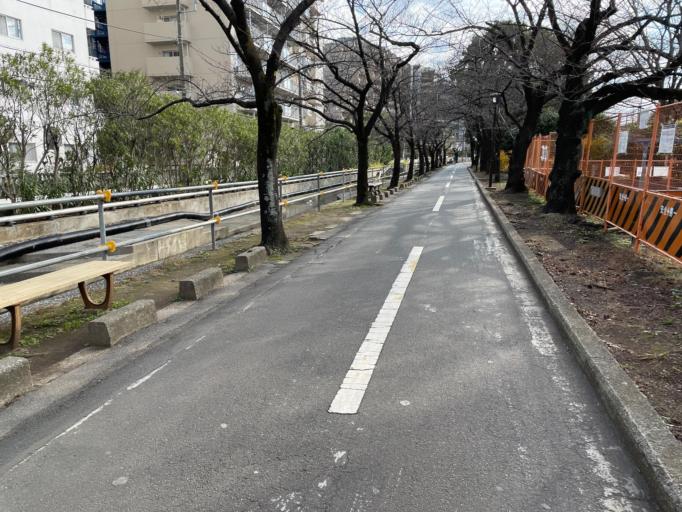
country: JP
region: Tokyo
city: Urayasu
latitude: 35.6815
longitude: 139.8390
